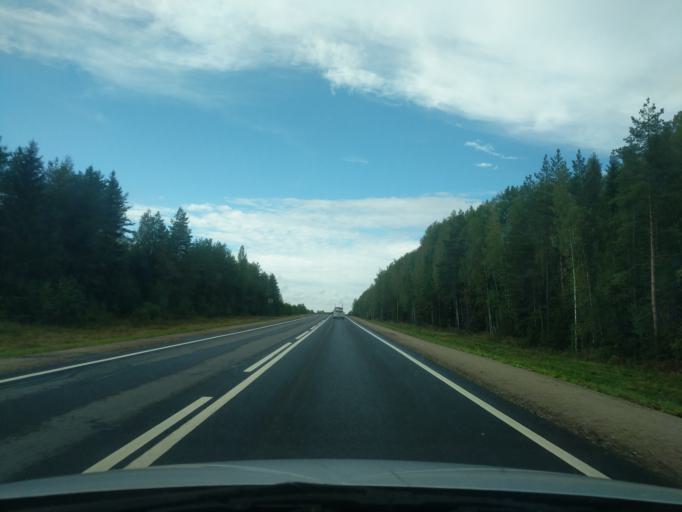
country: RU
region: Kostroma
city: Ostrovskoye
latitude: 57.8152
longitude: 41.9723
